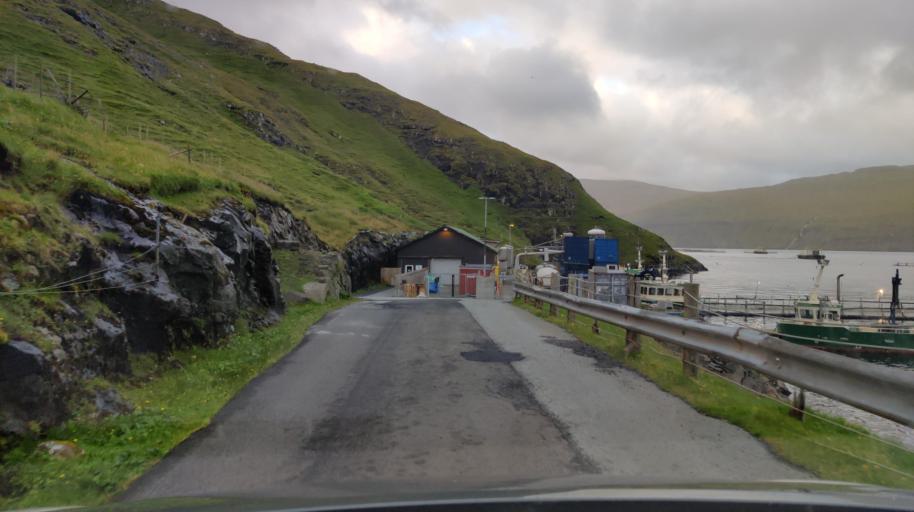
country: FO
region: Streymoy
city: Vestmanna
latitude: 62.1488
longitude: -7.1604
